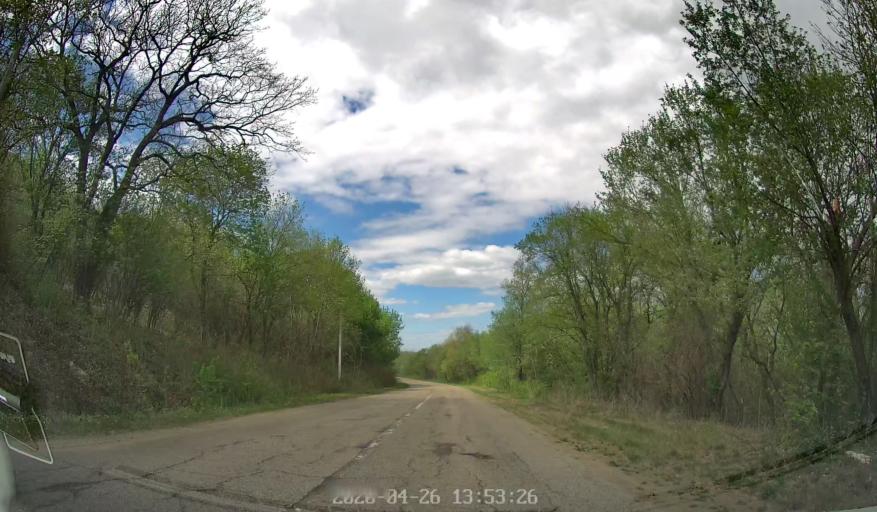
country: MD
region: Telenesti
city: Cocieri
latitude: 47.2790
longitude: 29.1096
